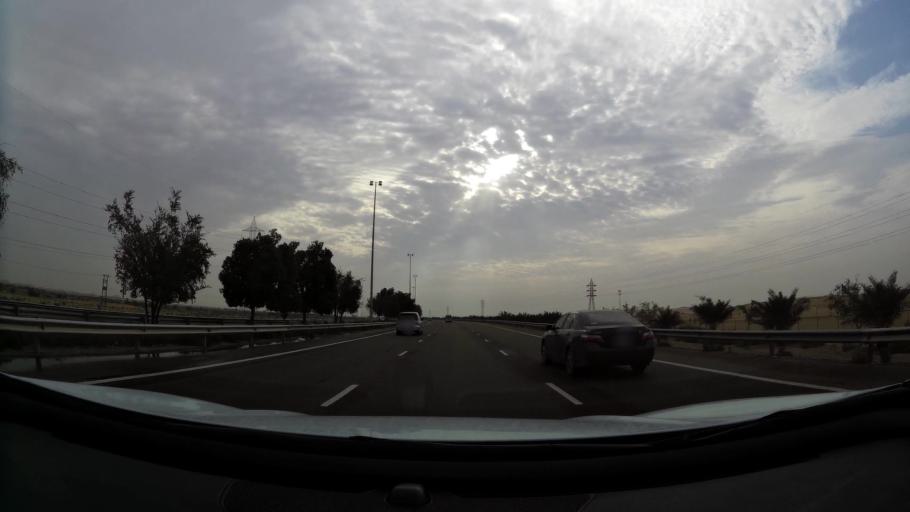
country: AE
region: Abu Dhabi
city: Abu Dhabi
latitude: 24.1964
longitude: 54.9268
